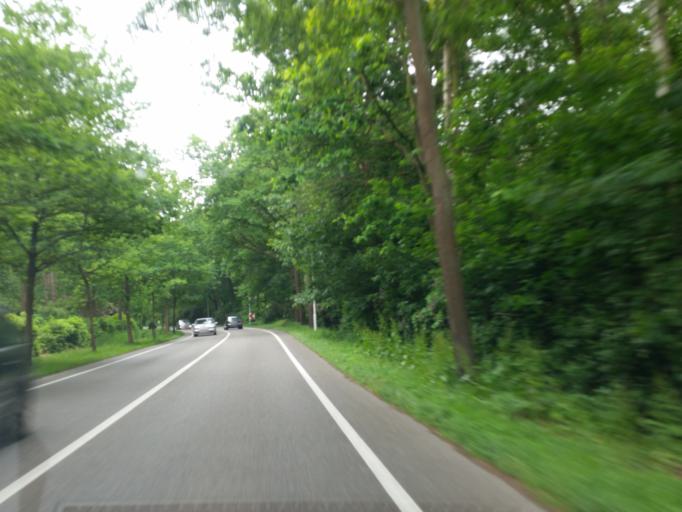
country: BE
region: Flanders
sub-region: Provincie Antwerpen
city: Schoten
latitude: 51.2711
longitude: 4.5302
